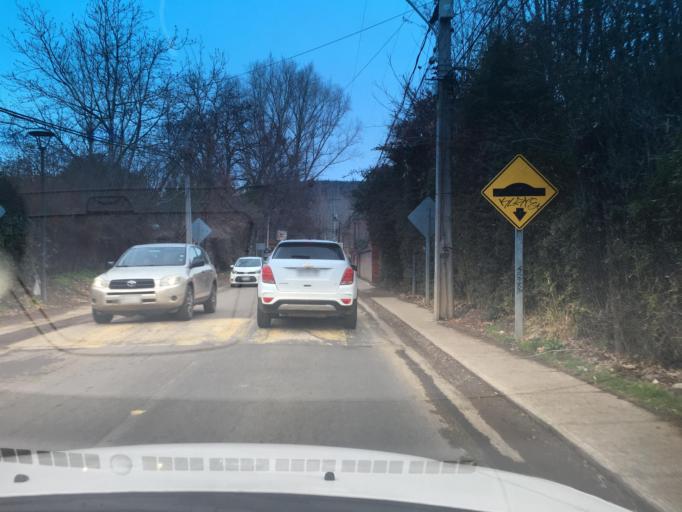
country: CL
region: Santiago Metropolitan
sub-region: Provincia de Cordillera
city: Puente Alto
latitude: -33.7289
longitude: -70.3170
